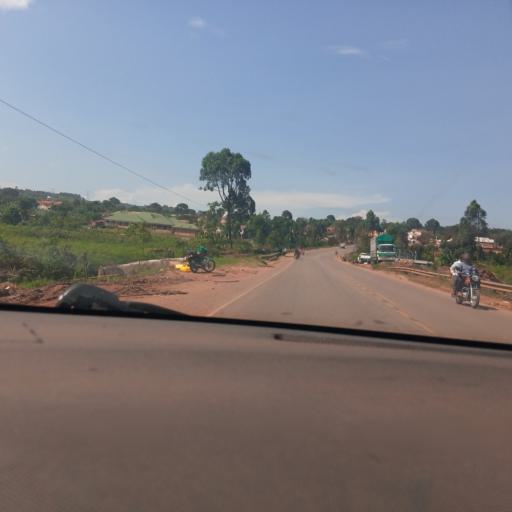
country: UG
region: Central Region
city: Masaka
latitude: -0.3099
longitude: 31.7529
